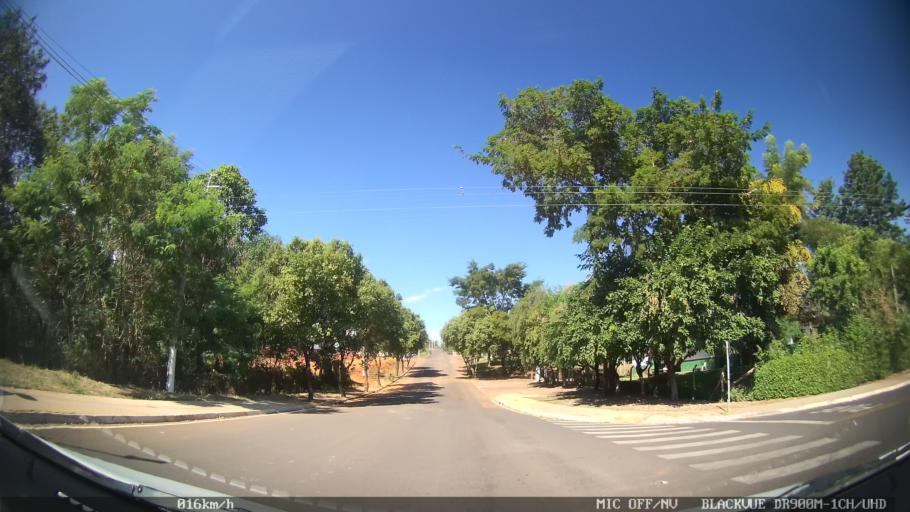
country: BR
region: Sao Paulo
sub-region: Santa Barbara D'Oeste
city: Santa Barbara d'Oeste
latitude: -22.7306
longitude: -47.4059
